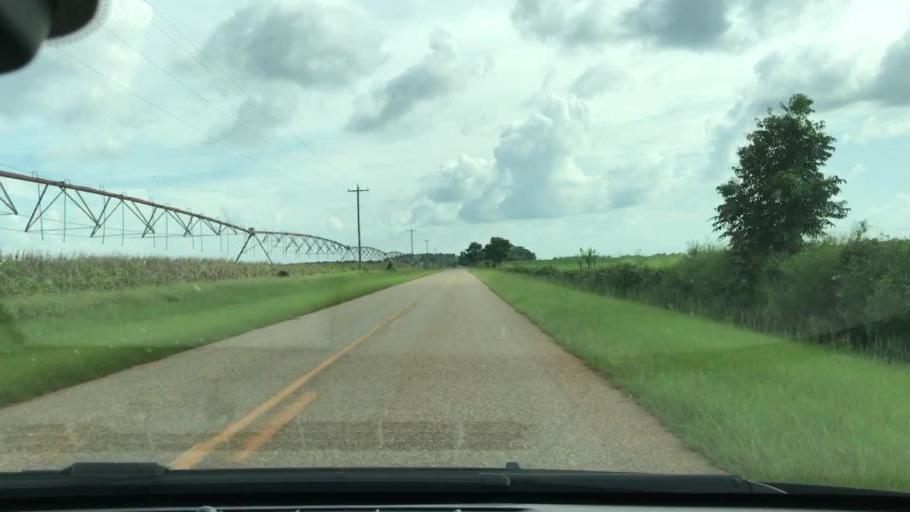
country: US
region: Georgia
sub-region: Clay County
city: Fort Gaines
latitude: 31.5294
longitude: -84.9544
